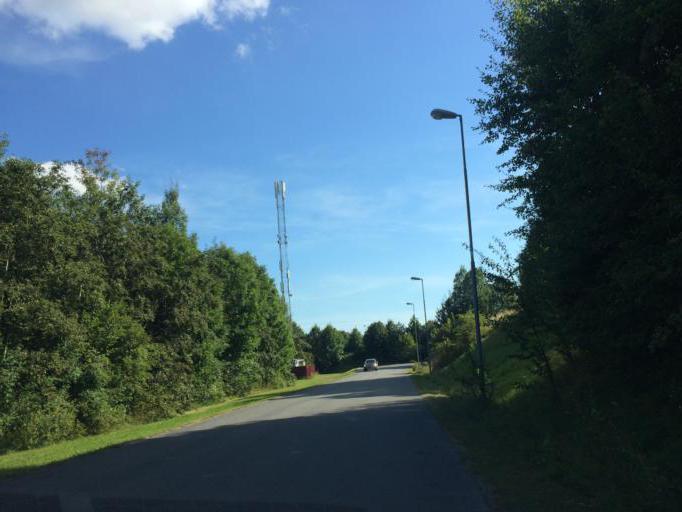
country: SE
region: Stockholm
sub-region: Sollentuna Kommun
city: Sollentuna
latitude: 59.4599
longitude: 17.9103
